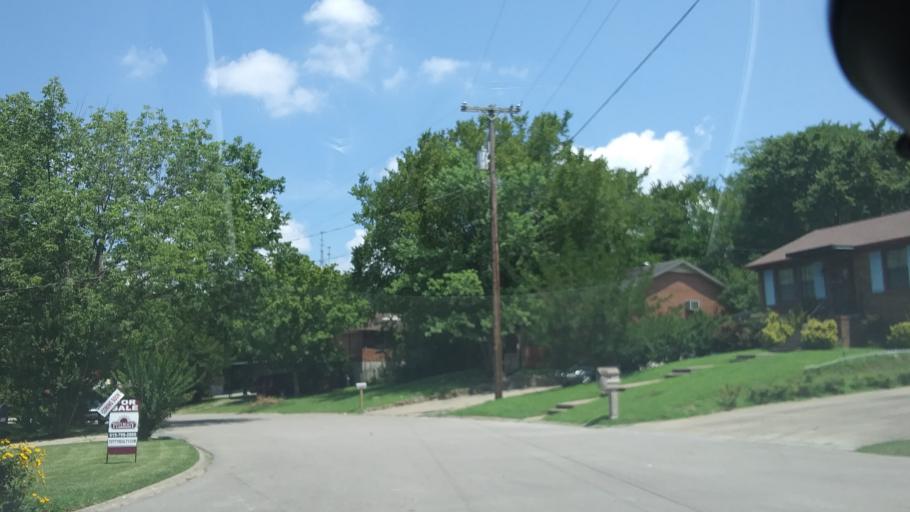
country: US
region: Tennessee
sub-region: Davidson County
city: Belle Meade
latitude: 36.0889
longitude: -86.9390
